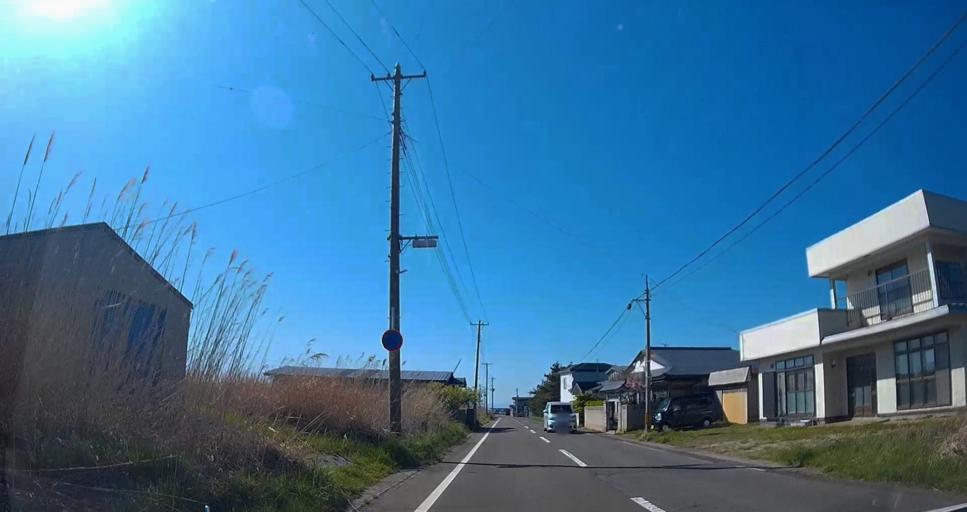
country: JP
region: Hokkaido
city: Hakodate
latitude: 41.5442
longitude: 140.9140
